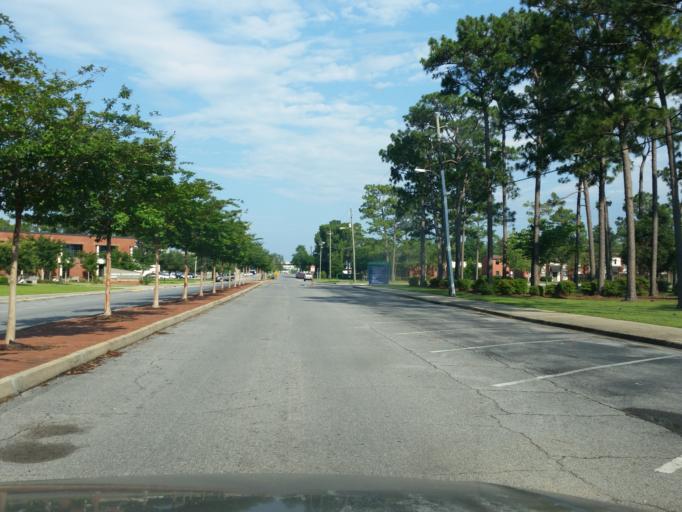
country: US
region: Florida
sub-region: Escambia County
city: Ferry Pass
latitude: 30.4793
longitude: -87.2019
